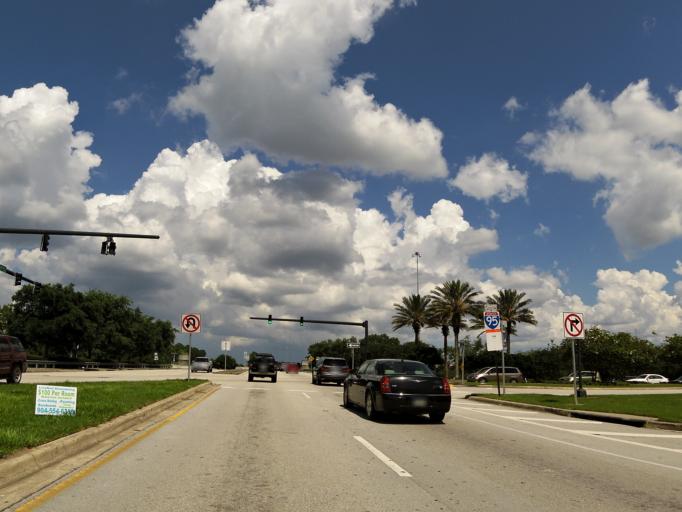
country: US
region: Florida
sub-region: Saint Johns County
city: Fruit Cove
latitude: 30.1415
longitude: -81.5427
